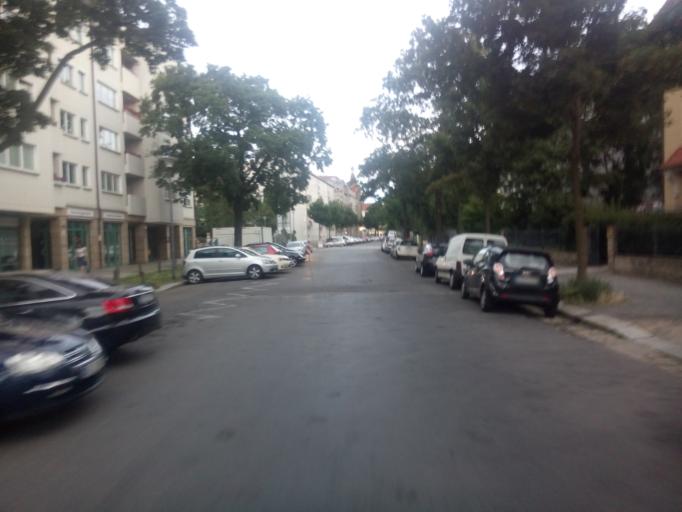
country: DE
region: Saxony
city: Albertstadt
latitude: 51.0477
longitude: 13.7768
